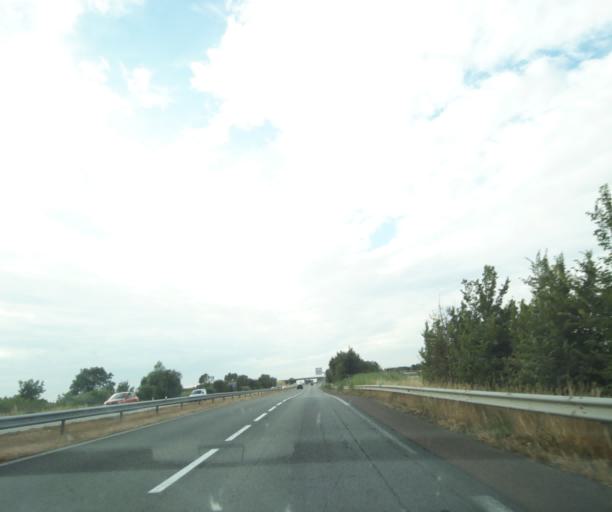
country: FR
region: Poitou-Charentes
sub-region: Departement de la Charente-Maritime
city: Chatelaillon-Plage
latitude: 46.0594
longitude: -1.0590
